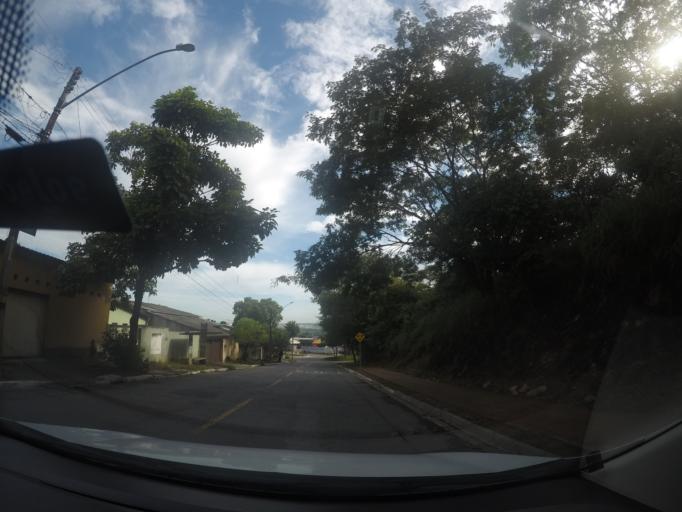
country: BR
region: Goias
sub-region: Goiania
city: Goiania
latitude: -16.6876
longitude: -49.2032
